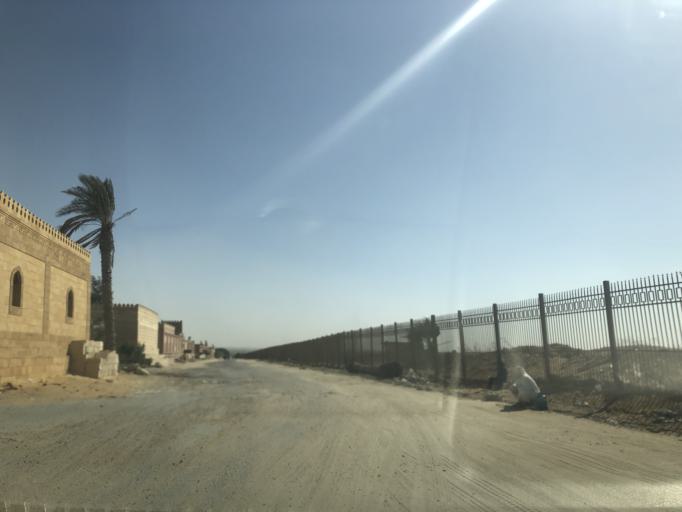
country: EG
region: Al Jizah
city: Madinat Sittah Uktubar
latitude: 29.9313
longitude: 30.9545
